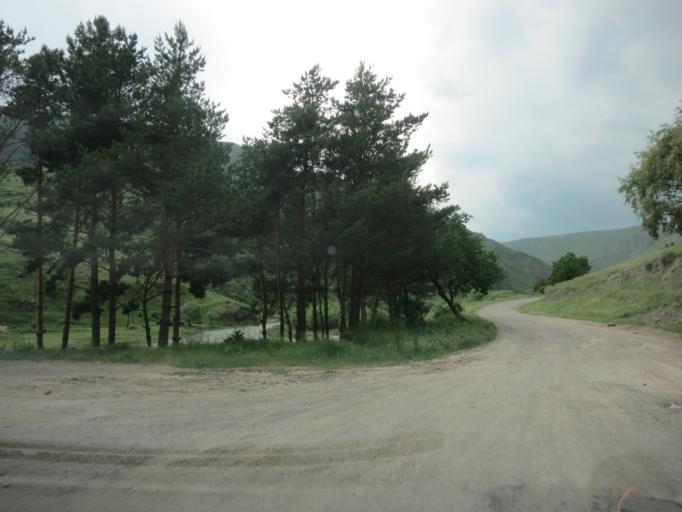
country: TR
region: Ardahan
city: Kurtkale
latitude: 41.3777
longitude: 43.2796
